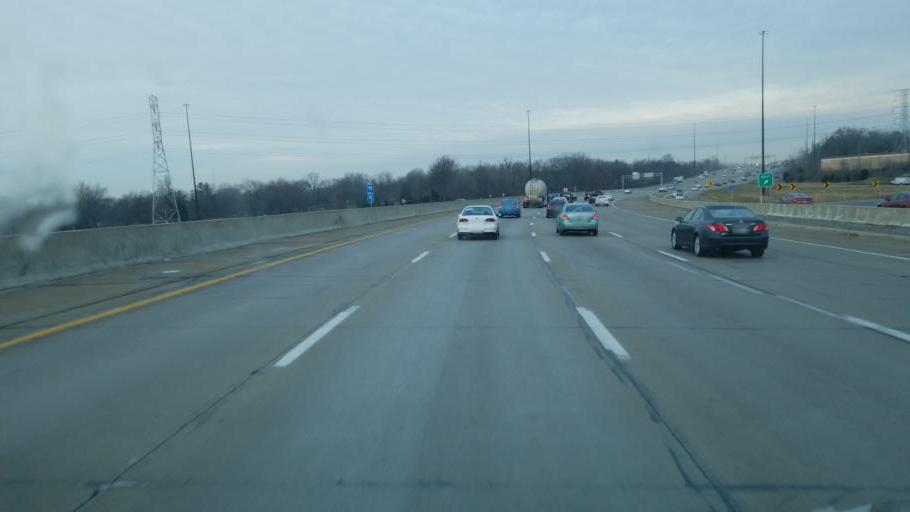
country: US
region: Indiana
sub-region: Marion County
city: Warren Park
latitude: 39.7988
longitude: -86.0464
